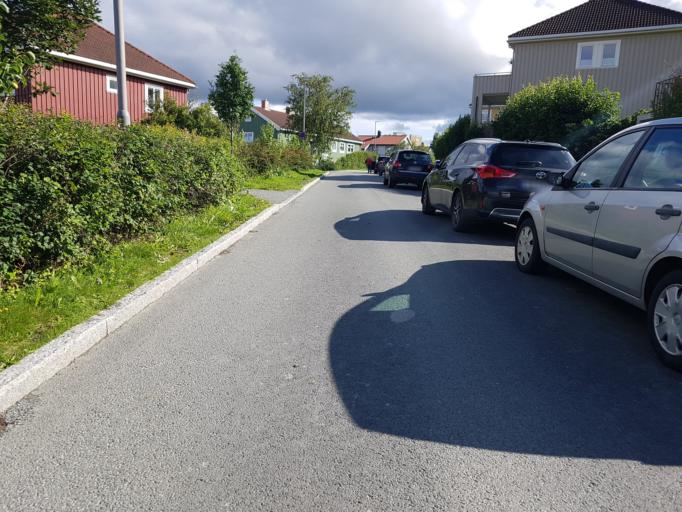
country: NO
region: Sor-Trondelag
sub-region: Trondheim
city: Trondheim
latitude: 63.4257
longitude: 10.4378
